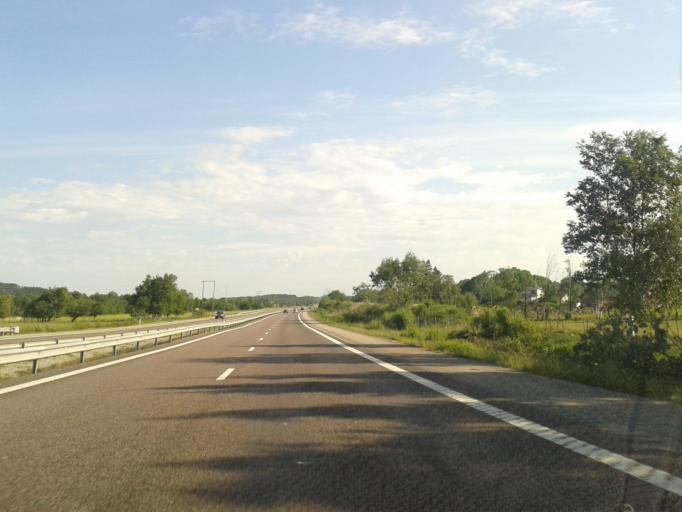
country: SE
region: Vaestra Goetaland
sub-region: Stenungsunds Kommun
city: Stora Hoga
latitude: 58.0111
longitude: 11.8434
